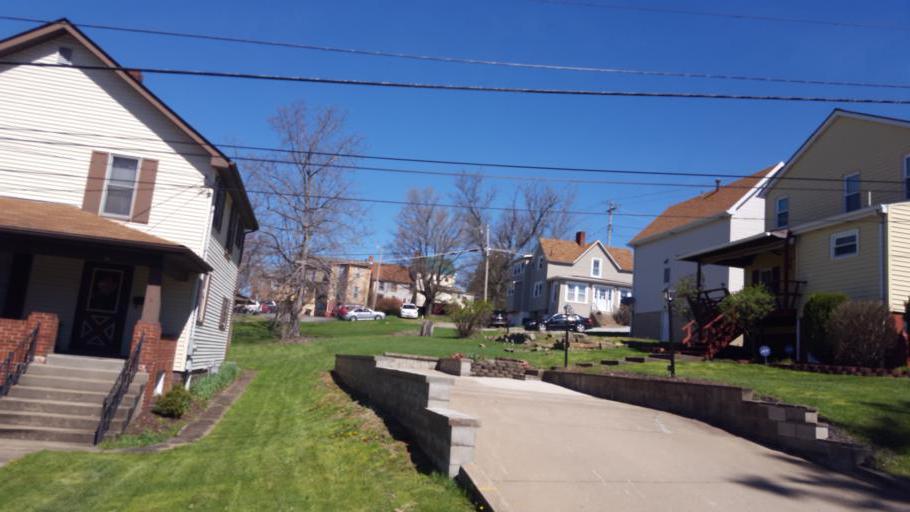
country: US
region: Ohio
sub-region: Belmont County
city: Saint Clairsville
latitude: 40.0799
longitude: -80.8978
